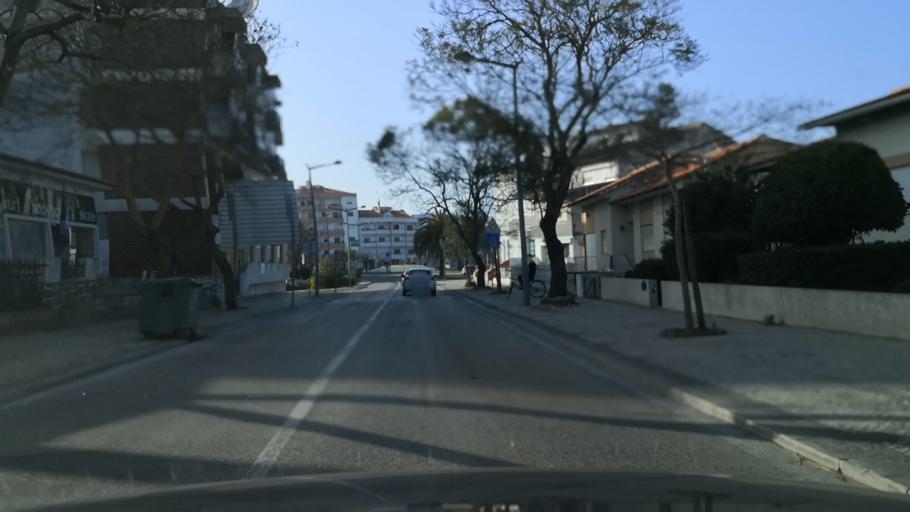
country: PT
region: Leiria
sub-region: Marinha Grande
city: Marinha Grande
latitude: 39.7471
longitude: -8.9350
